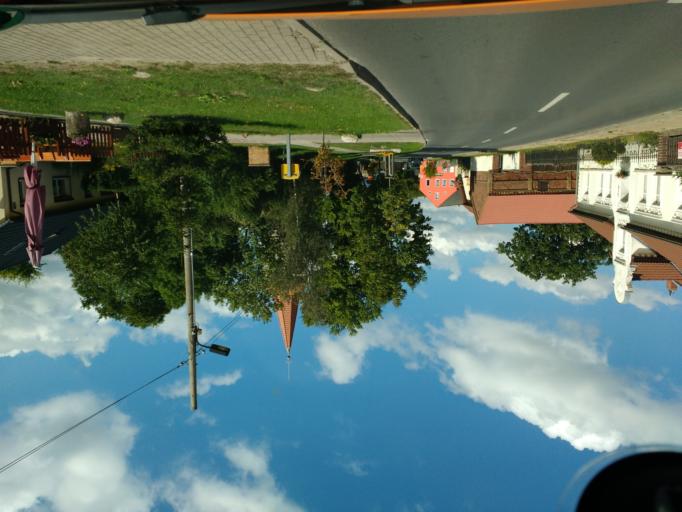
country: DE
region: Brandenburg
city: Wandlitz
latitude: 52.7292
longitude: 13.3865
